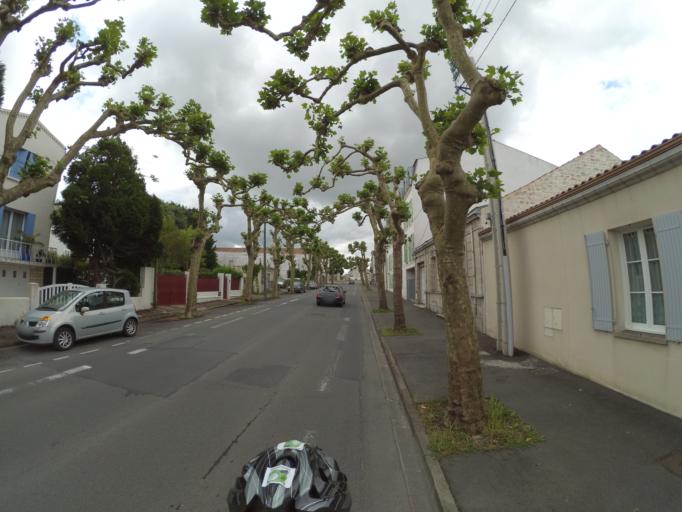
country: FR
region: Poitou-Charentes
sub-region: Departement de la Charente-Maritime
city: Rochefort
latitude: 45.9443
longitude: -0.9613
